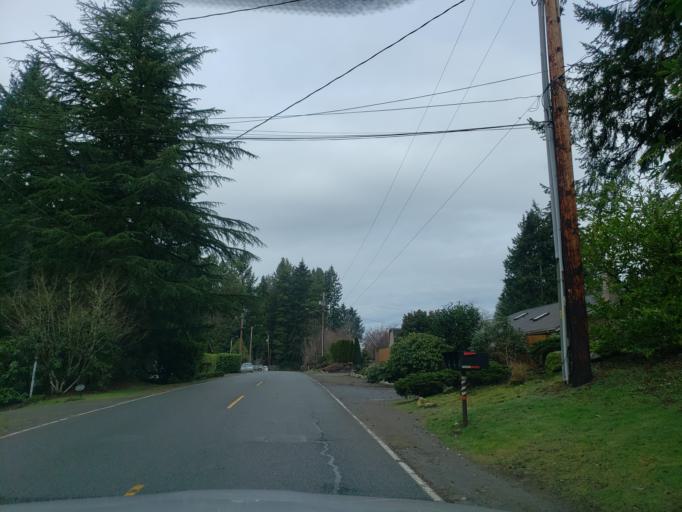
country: US
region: Washington
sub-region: Snohomish County
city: Lynnwood
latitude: 47.8162
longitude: -122.3426
